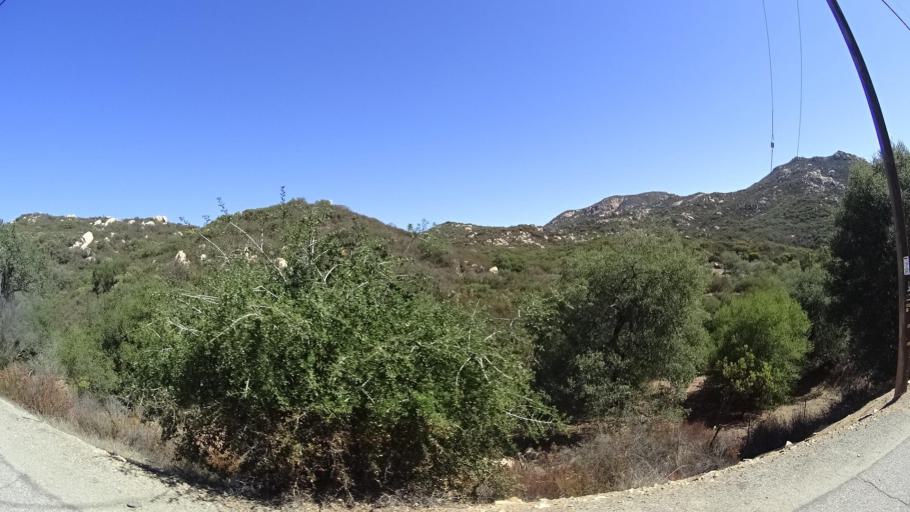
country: US
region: California
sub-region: San Diego County
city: Alpine
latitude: 32.7233
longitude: -116.7607
